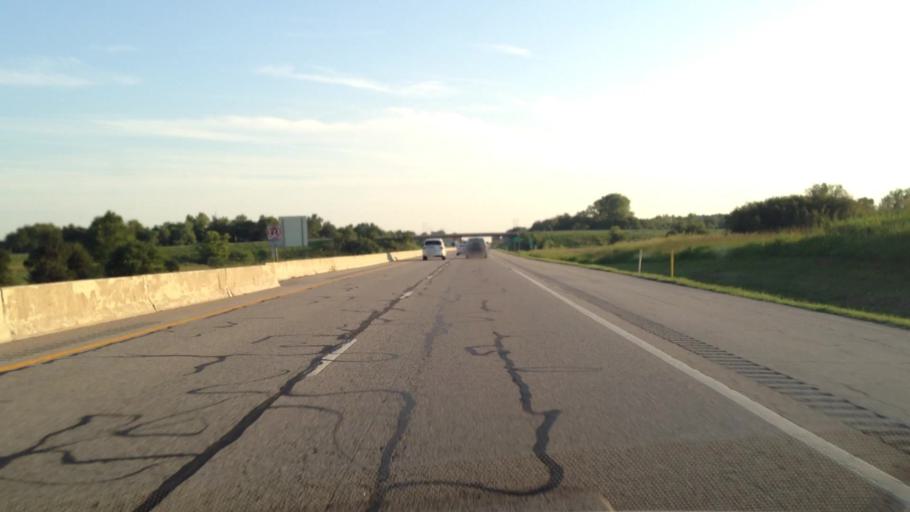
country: US
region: Oklahoma
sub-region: Ottawa County
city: Miami
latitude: 36.8480
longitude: -94.8580
